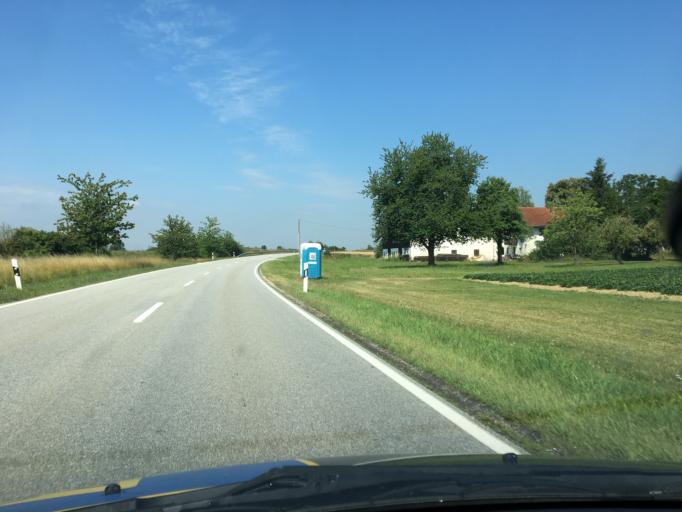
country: DE
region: Bavaria
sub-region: Upper Bavaria
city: Aresing
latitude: 48.2708
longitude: 12.5960
